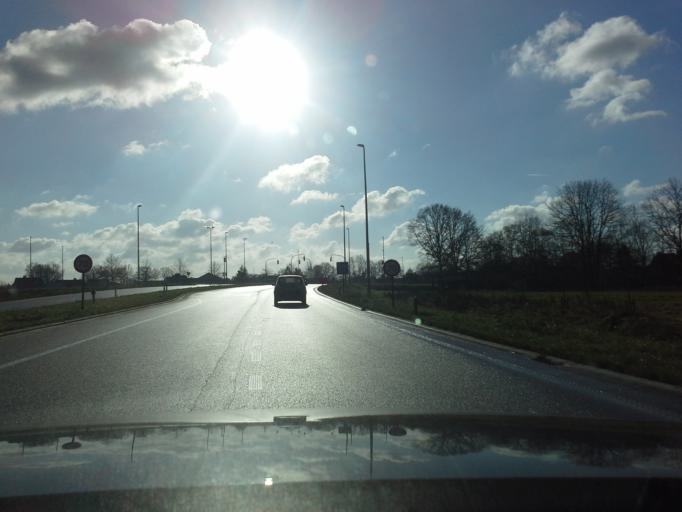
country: BE
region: Flanders
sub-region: Provincie Antwerpen
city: Geel
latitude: 51.1828
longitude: 4.9734
